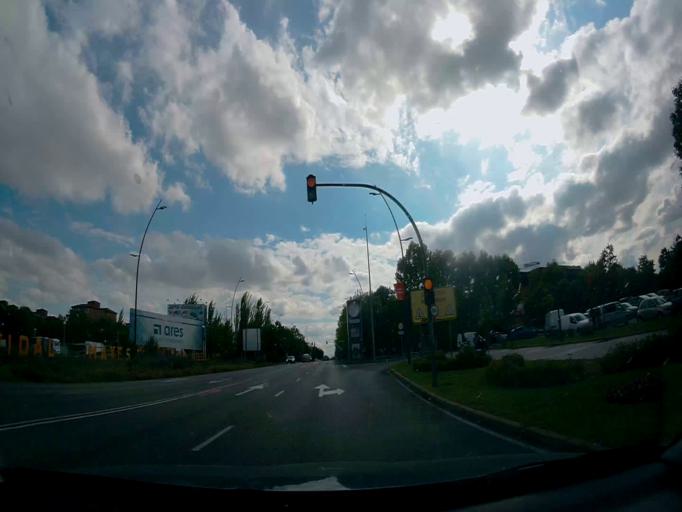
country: ES
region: Madrid
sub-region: Provincia de Madrid
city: Mostoles
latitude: 40.3318
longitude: -3.8547
